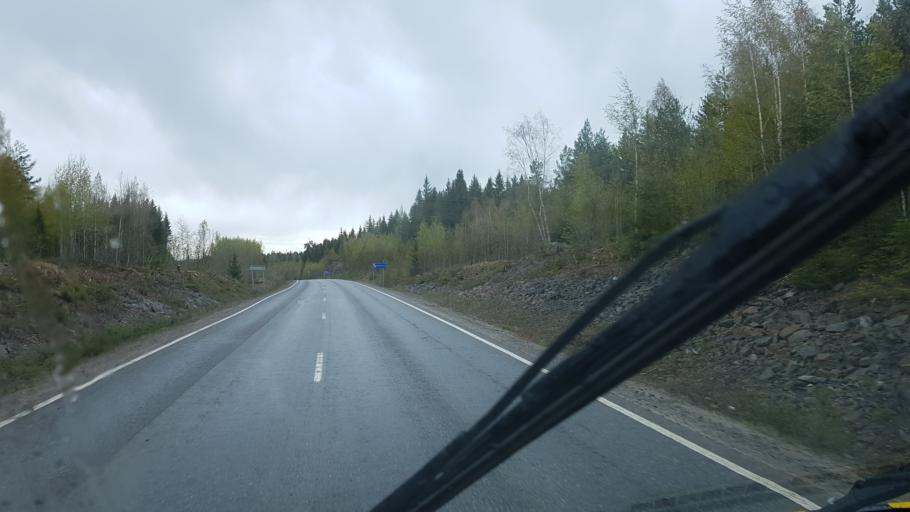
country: FI
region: Pirkanmaa
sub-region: Tampere
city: Pirkkala
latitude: 61.4047
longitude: 23.6323
